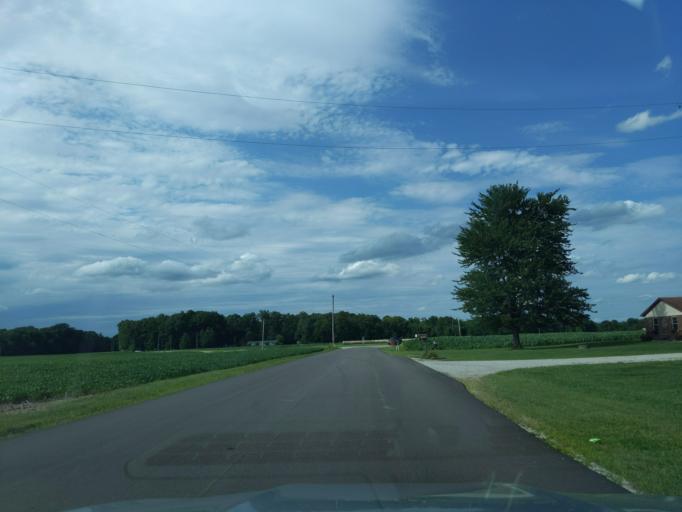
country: US
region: Indiana
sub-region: Ripley County
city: Sunman
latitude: 39.2843
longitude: -85.1014
